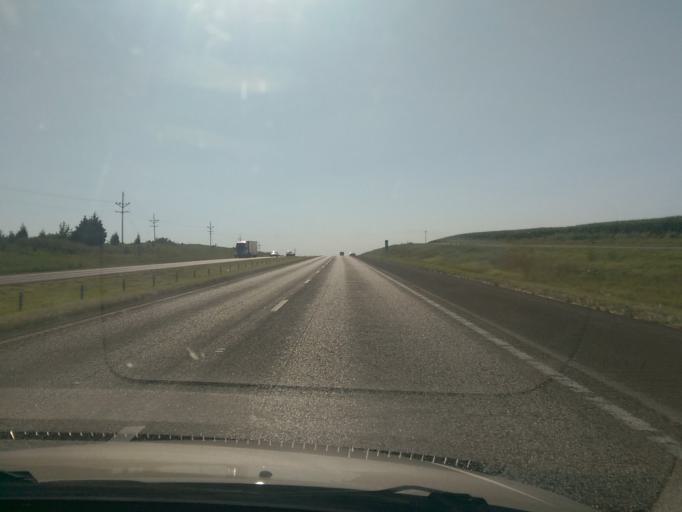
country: US
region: Missouri
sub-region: Lafayette County
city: Concordia
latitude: 38.9877
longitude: -93.5146
